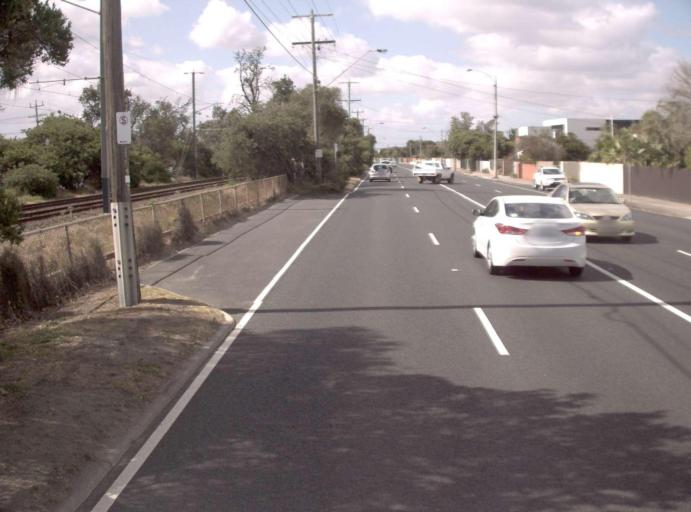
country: AU
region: Victoria
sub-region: Kingston
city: Bonbeach
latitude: -38.0650
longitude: 145.1199
